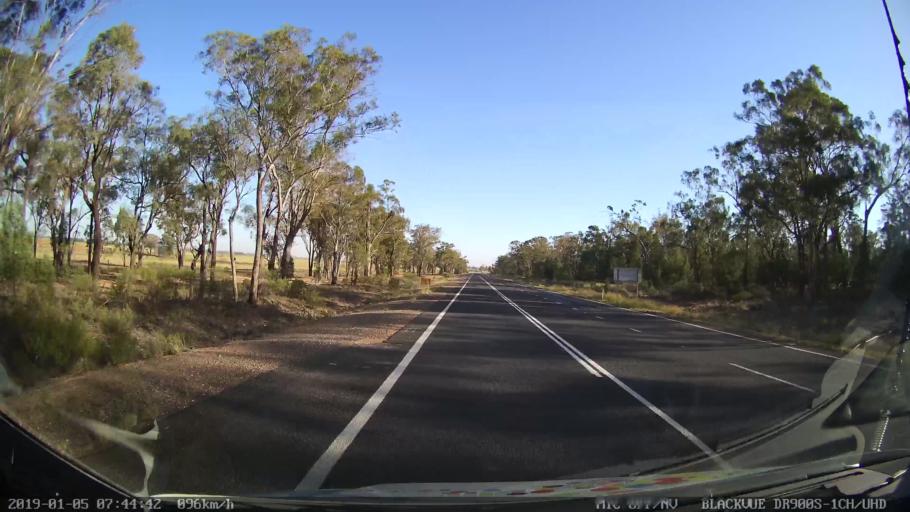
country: AU
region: New South Wales
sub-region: Gilgandra
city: Gilgandra
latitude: -31.8688
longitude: 148.6402
